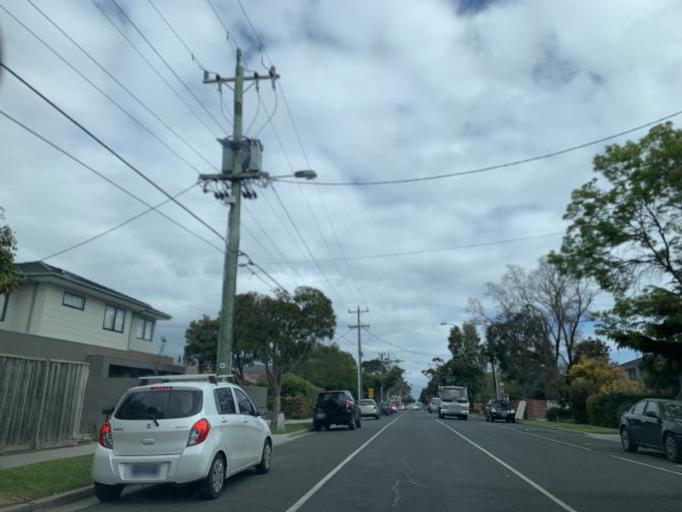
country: AU
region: Victoria
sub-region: Bayside
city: Cheltenham
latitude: -37.9774
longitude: 145.0535
